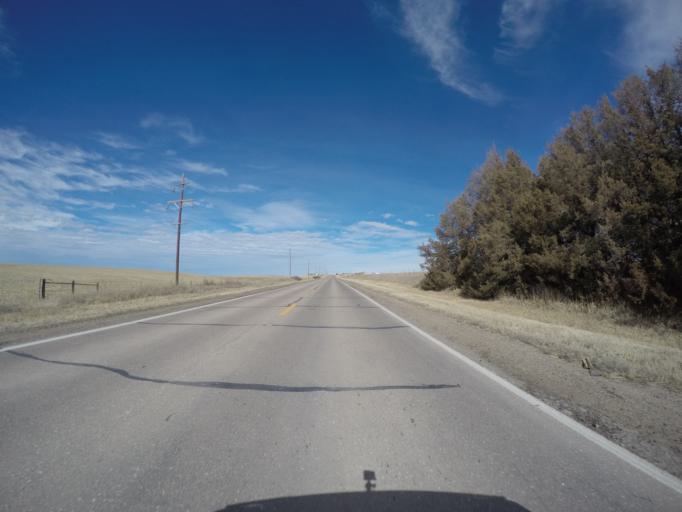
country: US
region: Nebraska
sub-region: Franklin County
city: Franklin
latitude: 40.1104
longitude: -98.9523
